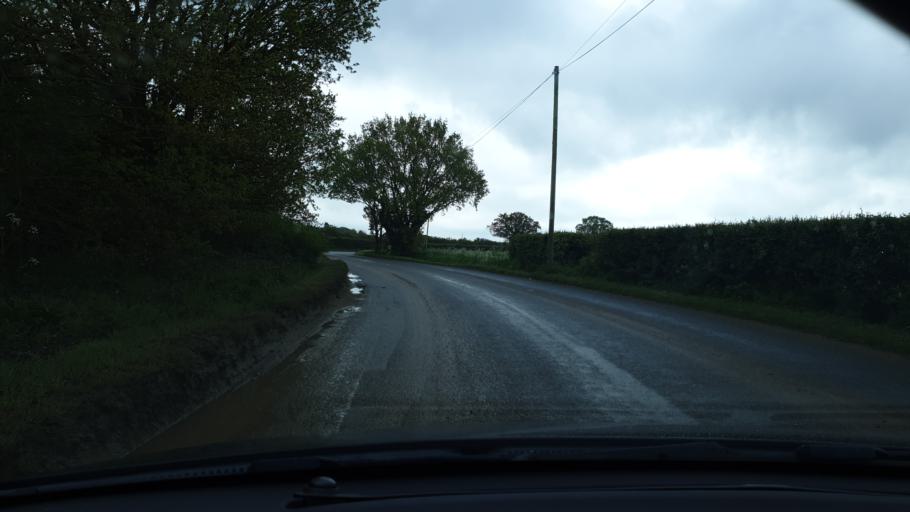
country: GB
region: England
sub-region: Essex
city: Wivenhoe
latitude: 51.9123
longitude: 0.9776
